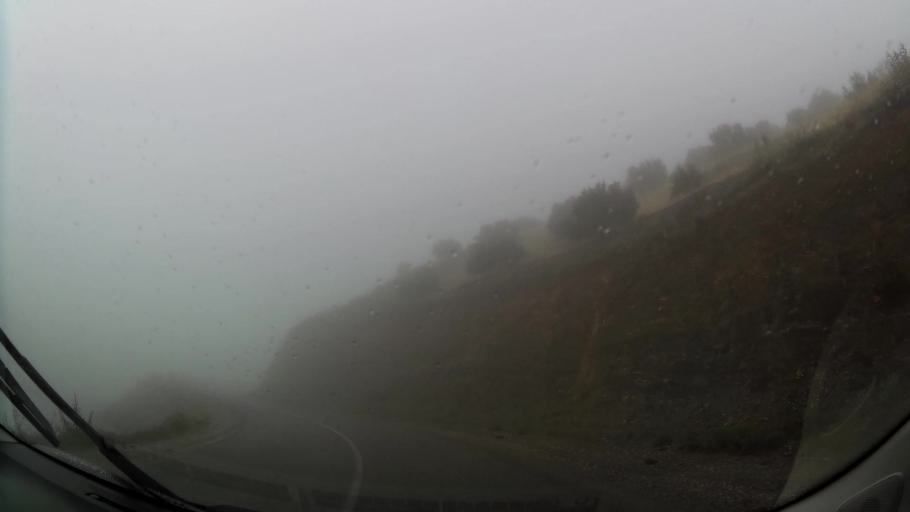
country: MA
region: Oriental
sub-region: Nador
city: Boudinar
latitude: 35.0993
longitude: -3.5498
